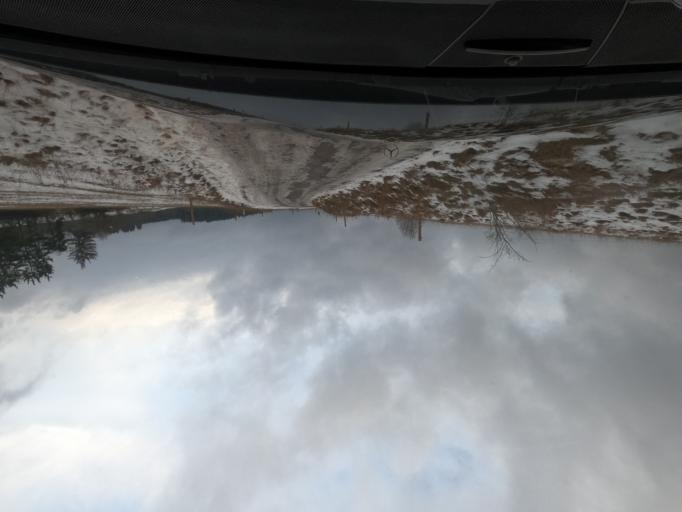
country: DE
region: Thuringia
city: Finsterbergen
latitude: 50.8282
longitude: 10.5925
